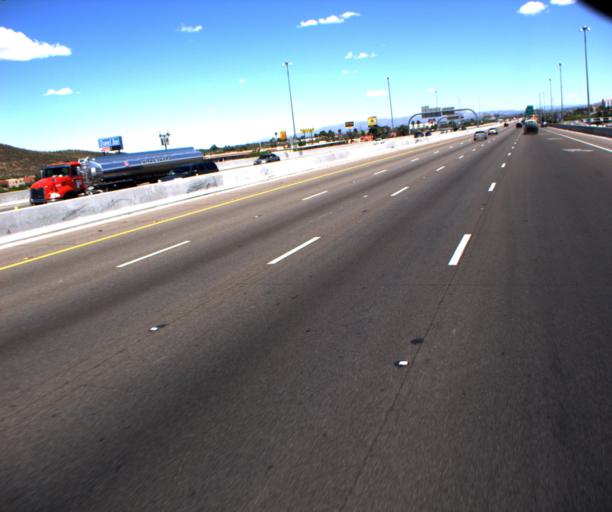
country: US
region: Arizona
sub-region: Pima County
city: South Tucson
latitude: 32.2030
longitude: -110.9794
